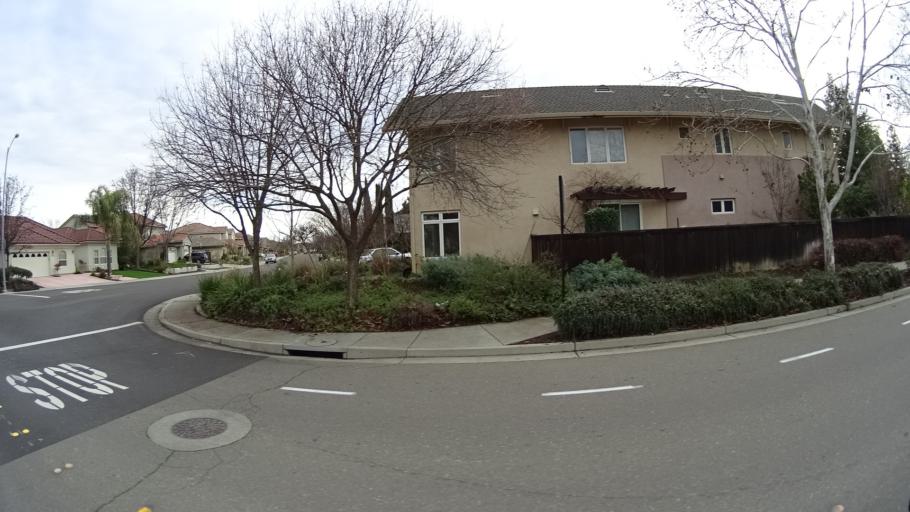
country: US
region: California
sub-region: Yolo County
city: Davis
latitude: 38.5698
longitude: -121.7172
